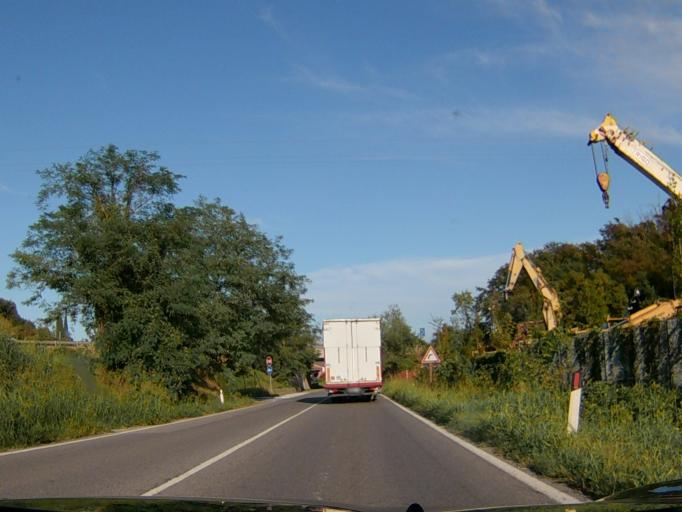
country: IT
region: Lombardy
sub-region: Provincia di Brescia
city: Lonato
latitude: 45.4622
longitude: 10.5059
